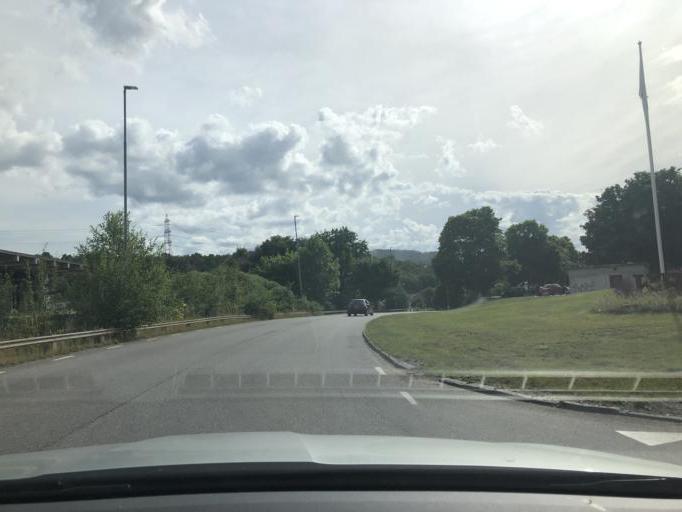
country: SE
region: Stockholm
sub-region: Botkyrka Kommun
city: Fittja
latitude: 59.2472
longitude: 17.8599
